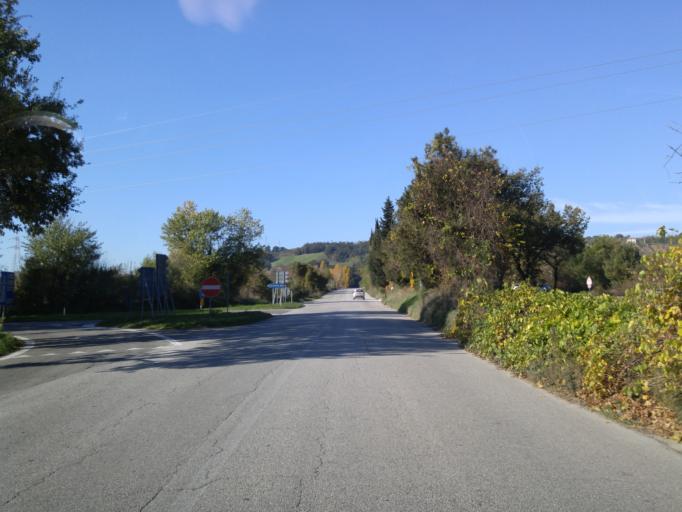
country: IT
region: The Marches
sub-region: Provincia di Pesaro e Urbino
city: Tavernelle
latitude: 43.7264
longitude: 12.8922
